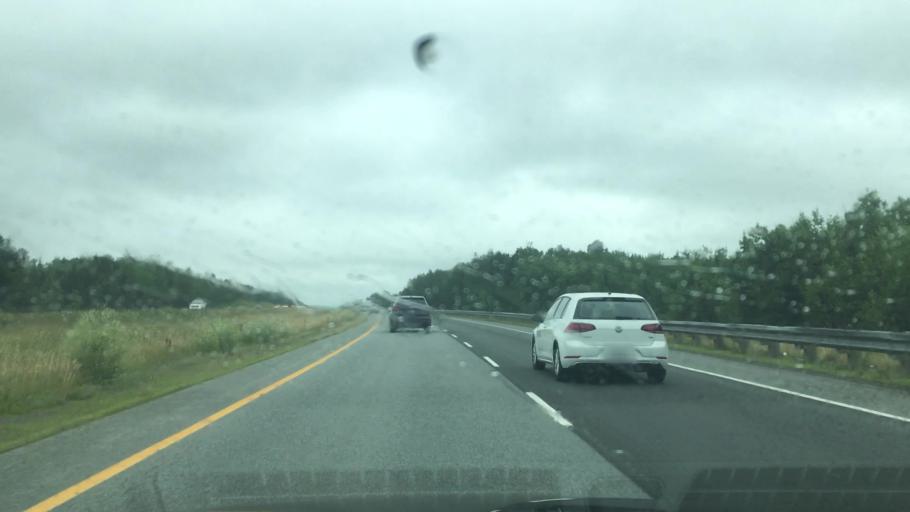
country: CA
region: Nova Scotia
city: Truro
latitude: 45.2693
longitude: -63.2925
